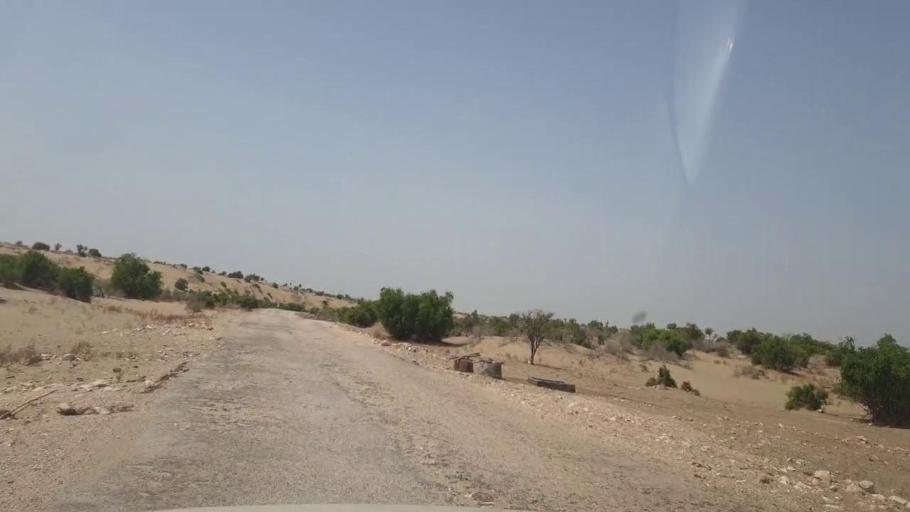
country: PK
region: Sindh
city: Khanpur
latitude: 27.3704
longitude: 69.3183
